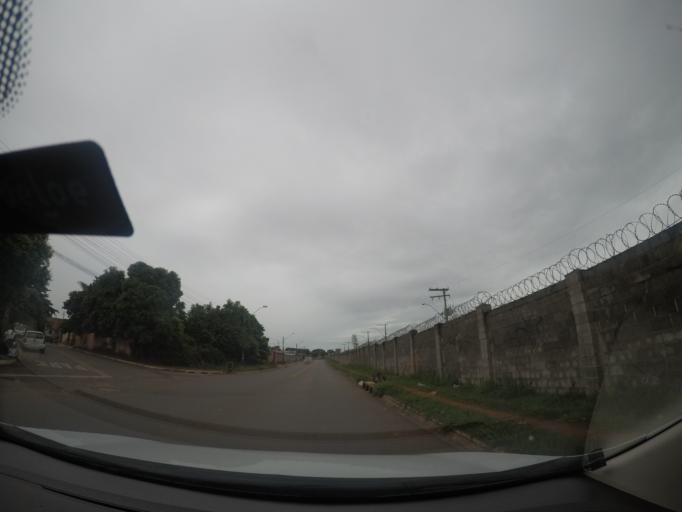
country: BR
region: Goias
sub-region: Goiania
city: Goiania
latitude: -16.6092
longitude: -49.3480
